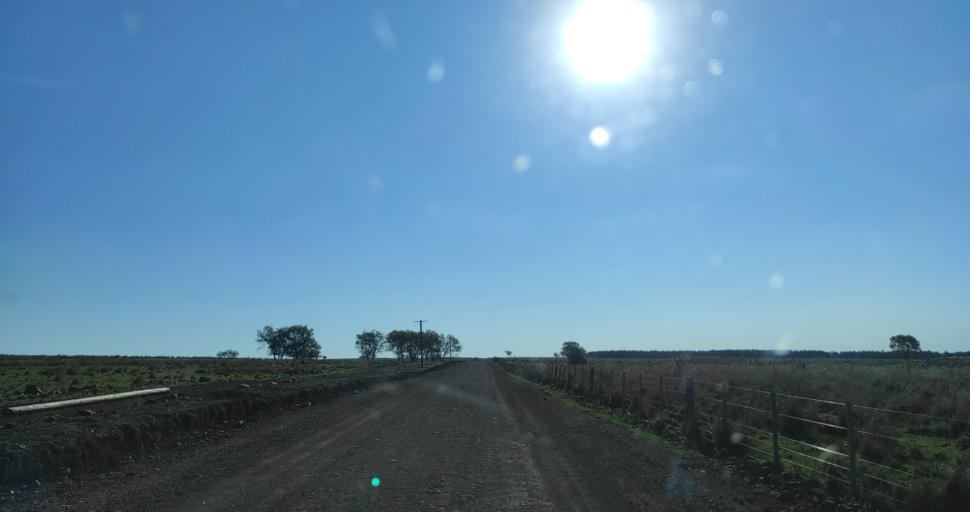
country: PY
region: Itapua
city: San Juan del Parana
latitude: -27.4182
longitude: -56.1263
